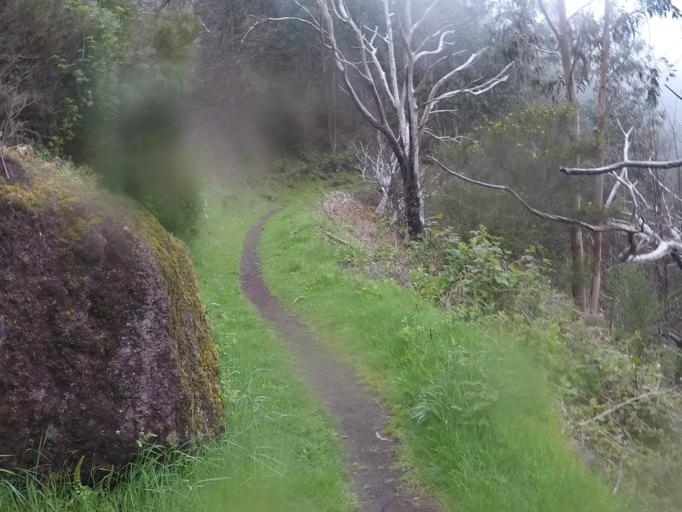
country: PT
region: Madeira
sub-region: Camara de Lobos
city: Curral das Freiras
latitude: 32.7253
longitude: -16.9845
